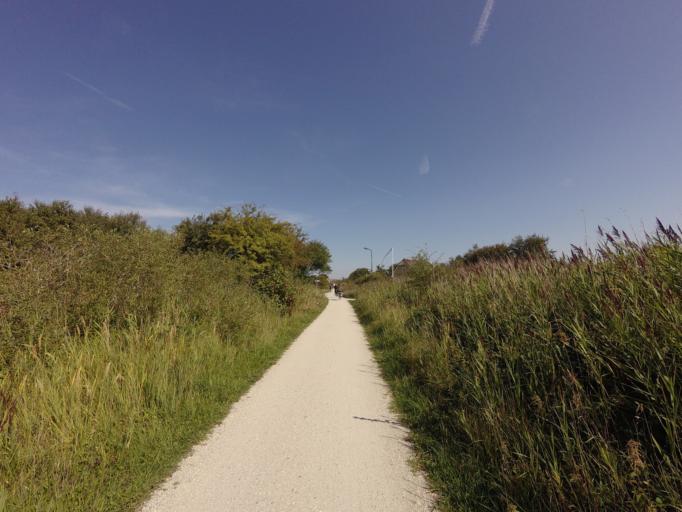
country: NL
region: Friesland
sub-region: Gemeente Schiermonnikoog
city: Schiermonnikoog
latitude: 53.4860
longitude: 6.1497
